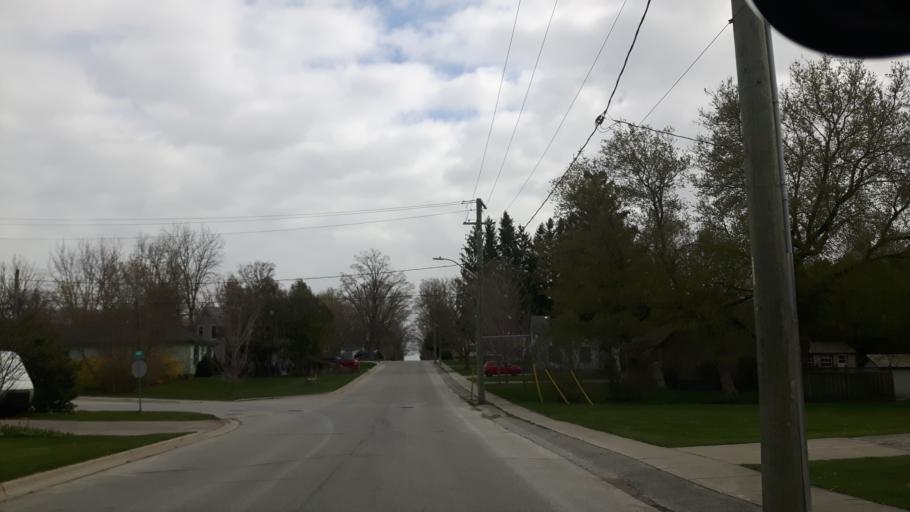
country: CA
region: Ontario
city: Bluewater
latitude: 43.6179
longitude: -81.5451
